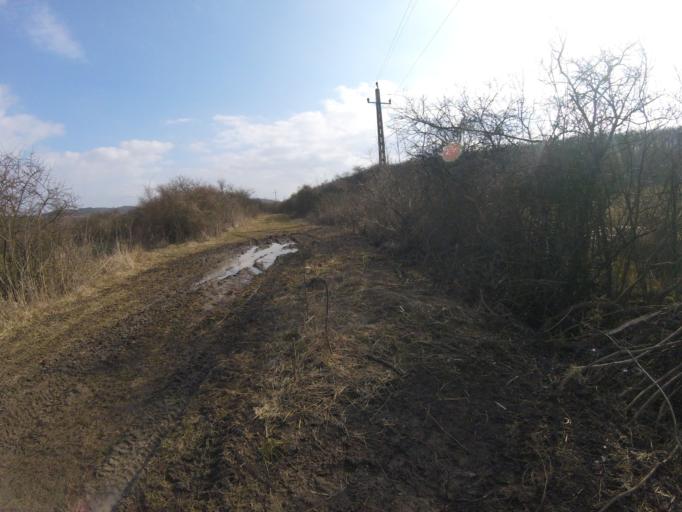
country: HU
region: Heves
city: Egerszalok
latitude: 47.8493
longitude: 20.3233
